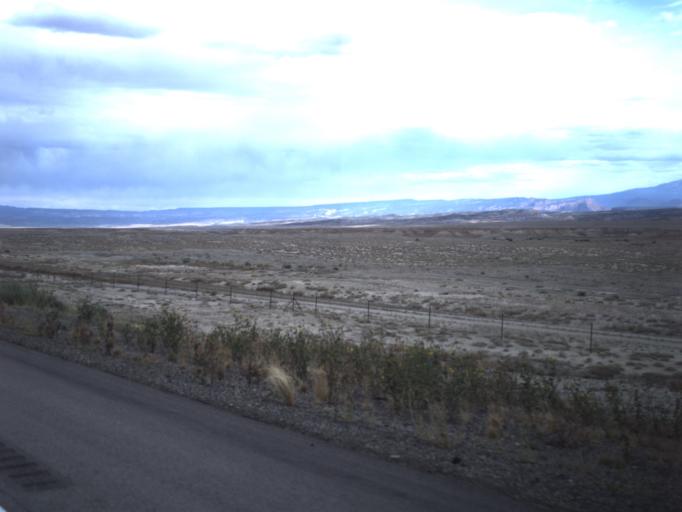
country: US
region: Utah
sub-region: Grand County
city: Moab
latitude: 38.9333
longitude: -109.4488
